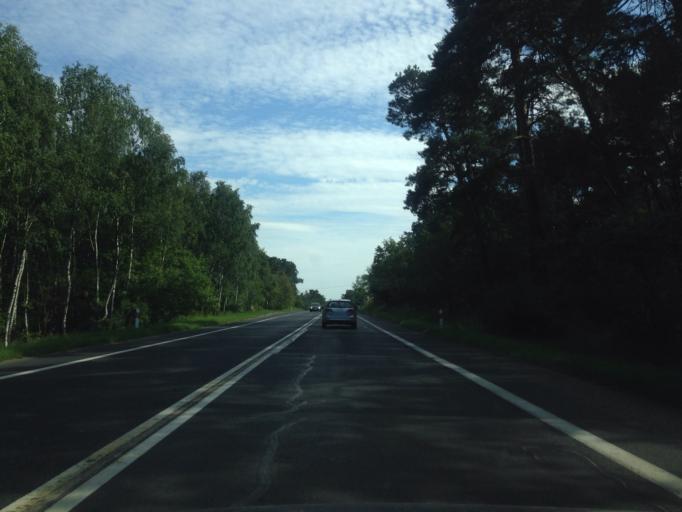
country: PL
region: Kujawsko-Pomorskie
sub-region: Powiat aleksandrowski
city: Aleksandrow Kujawski
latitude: 52.9637
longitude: 18.6845
